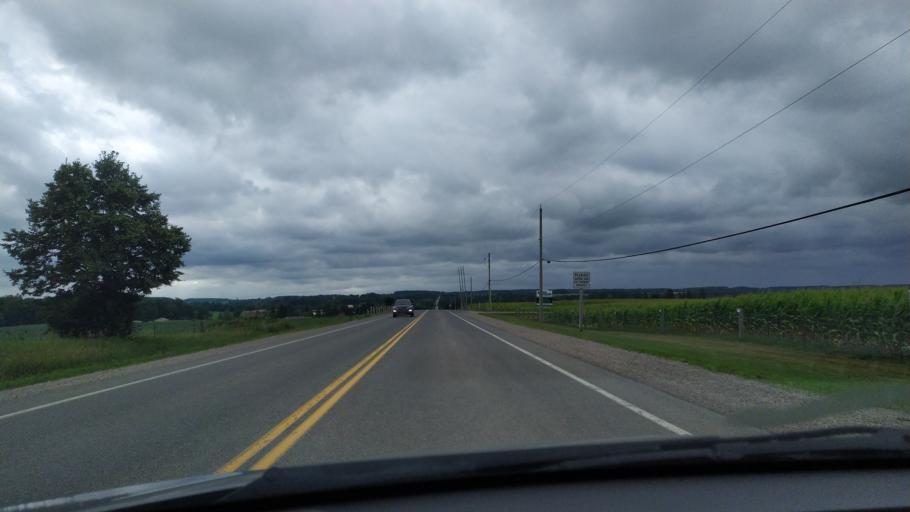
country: CA
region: Ontario
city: Kitchener
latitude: 43.3533
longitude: -80.5105
